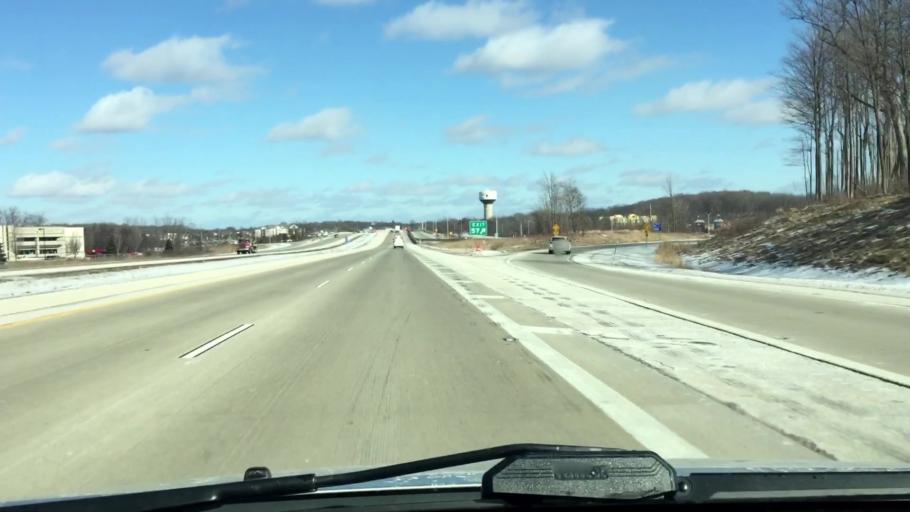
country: US
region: Wisconsin
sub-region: Waukesha County
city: New Berlin
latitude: 42.9485
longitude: -88.1142
